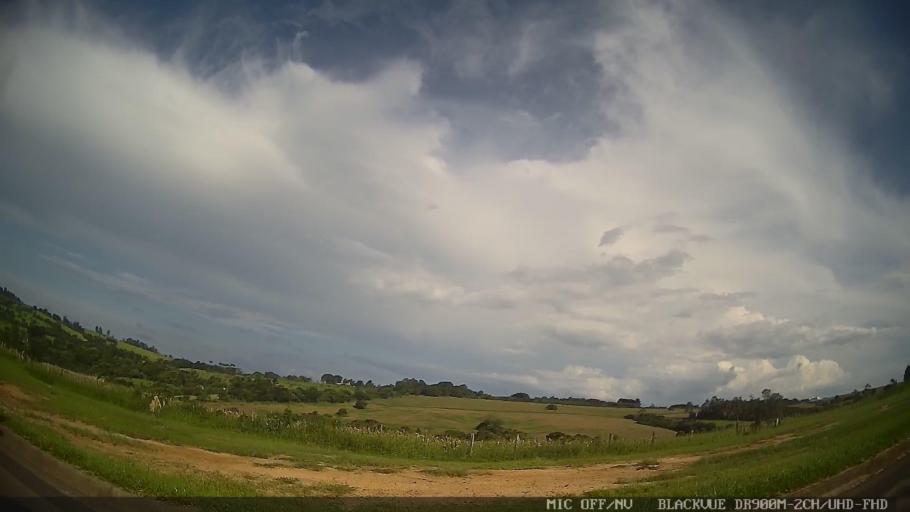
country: BR
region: Sao Paulo
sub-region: Tiete
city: Tiete
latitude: -23.1166
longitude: -47.6990
